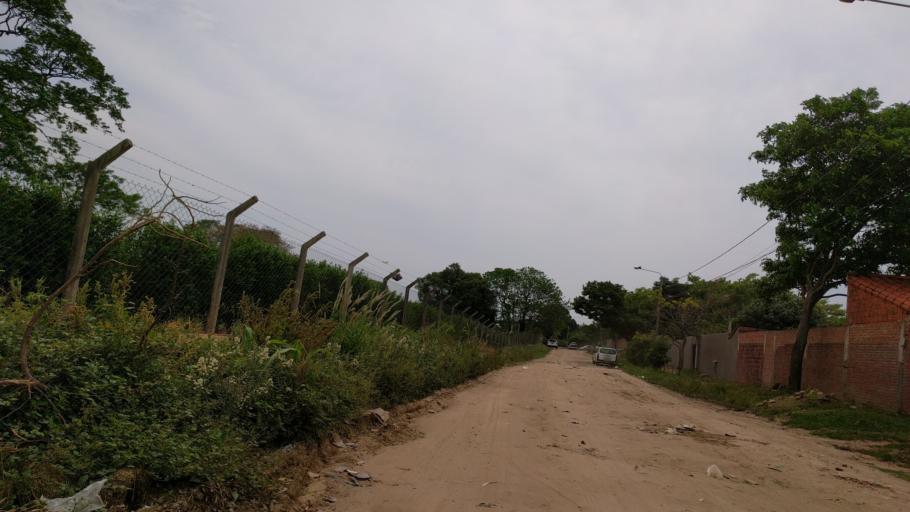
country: BO
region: Santa Cruz
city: Santa Cruz de la Sierra
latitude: -17.8146
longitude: -63.2320
